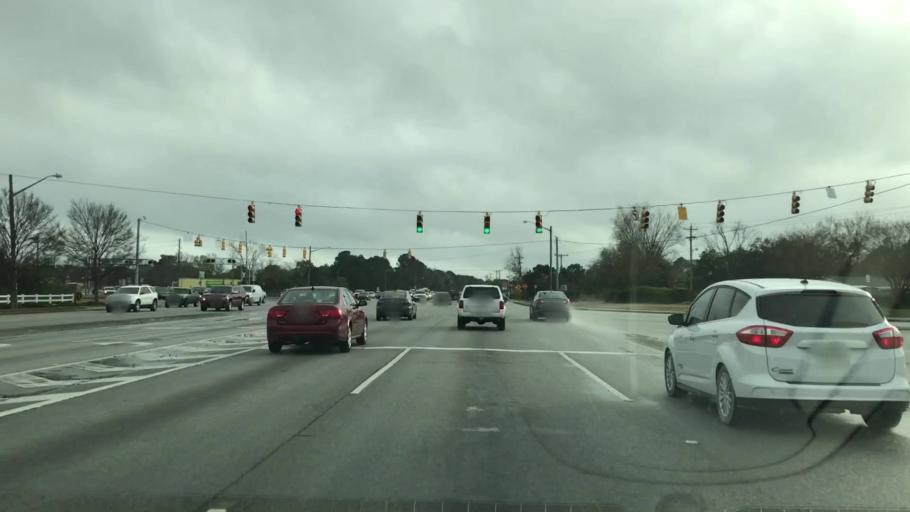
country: US
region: South Carolina
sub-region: Berkeley County
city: Goose Creek
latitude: 32.9960
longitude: -80.0346
